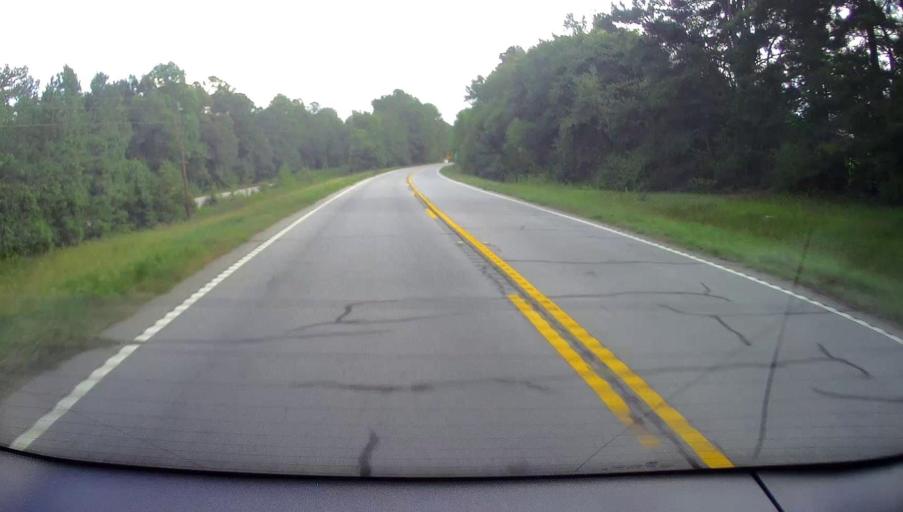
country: US
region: Georgia
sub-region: Meriwether County
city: Greenville
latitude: 33.0280
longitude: -84.5625
